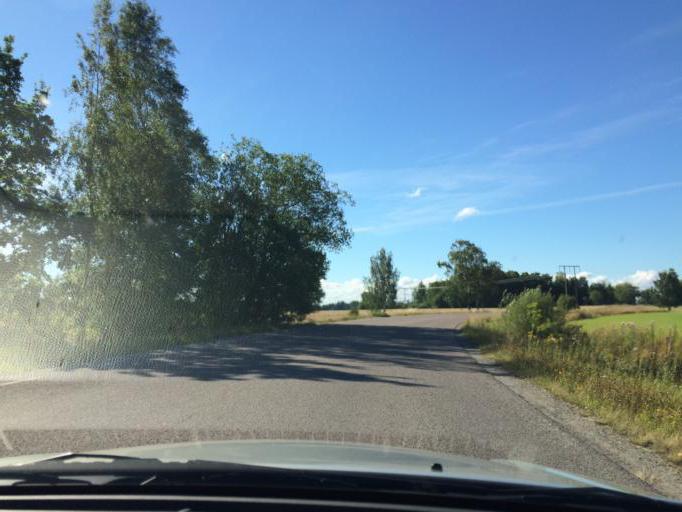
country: SE
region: Vaestmanland
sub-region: Vasteras
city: Tillberga
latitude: 59.6251
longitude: 16.6262
